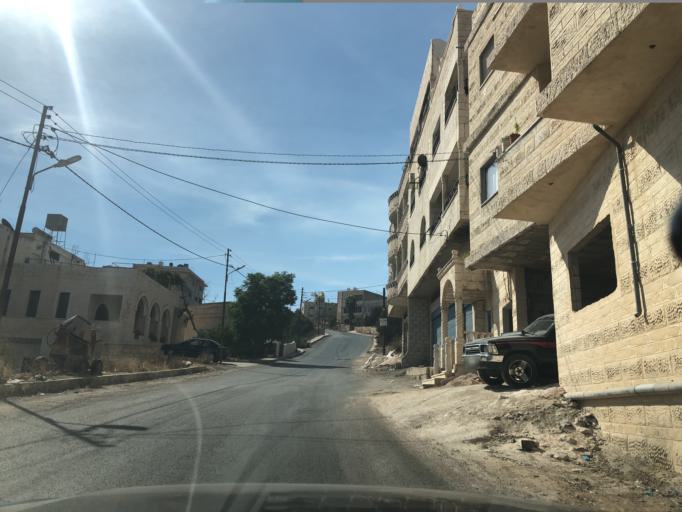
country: JO
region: Ajlun
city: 'Ajlun
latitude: 32.3310
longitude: 35.7433
